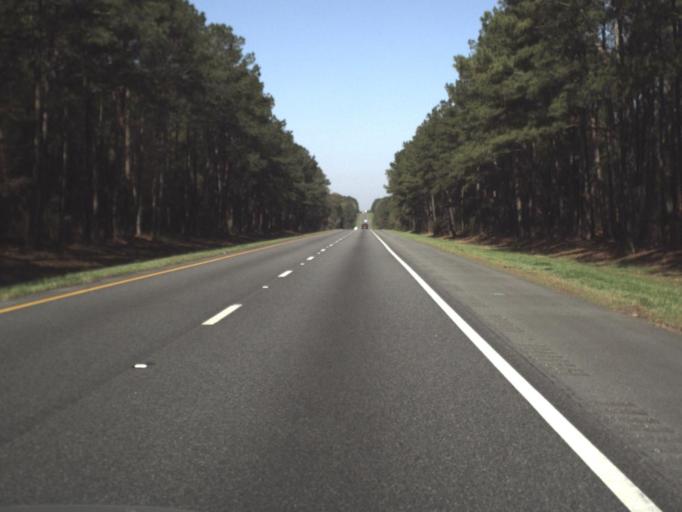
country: US
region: Florida
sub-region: Gadsden County
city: Midway
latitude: 30.5146
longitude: -84.4756
